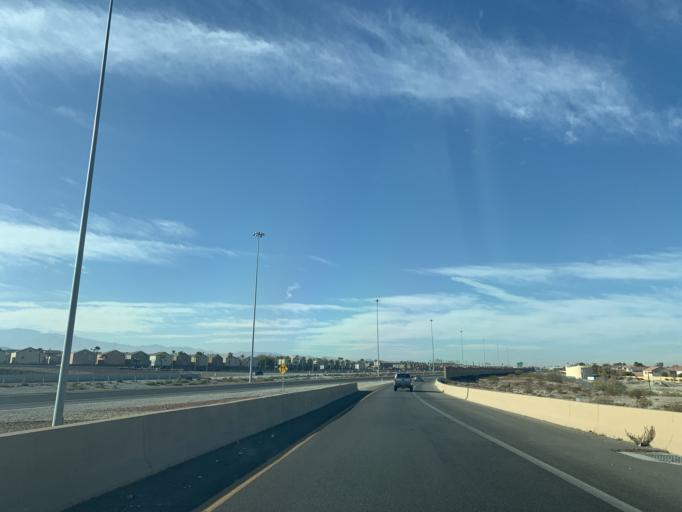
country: US
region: Nevada
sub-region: Clark County
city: Summerlin South
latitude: 36.3003
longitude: -115.2866
